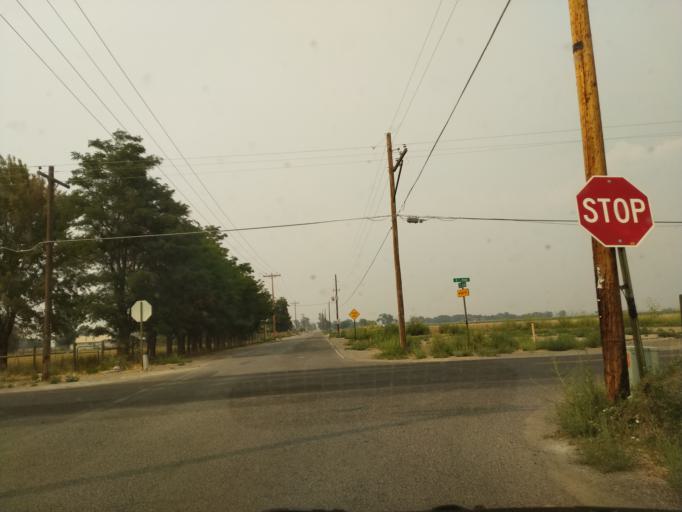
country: US
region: Colorado
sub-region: Mesa County
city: Fruitvale
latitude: 39.0410
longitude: -108.4968
